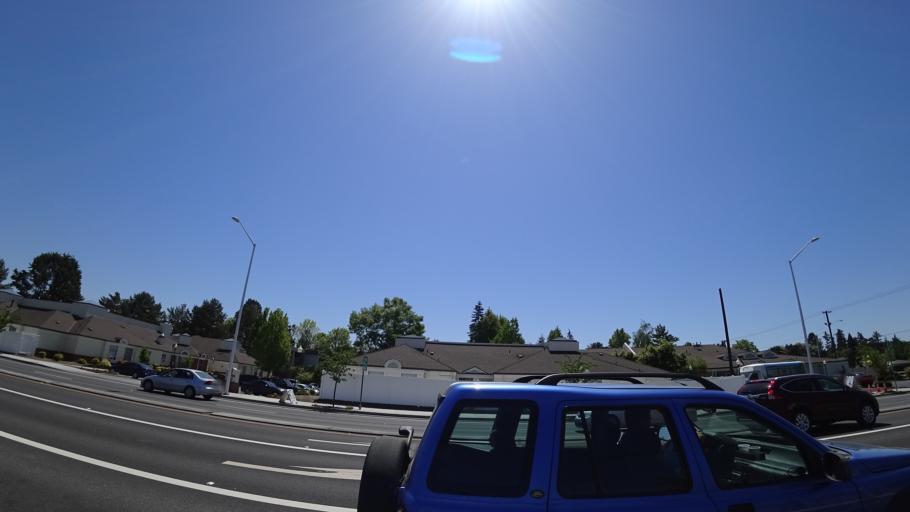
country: US
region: Oregon
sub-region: Washington County
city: Beaverton
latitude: 45.4860
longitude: -122.8251
